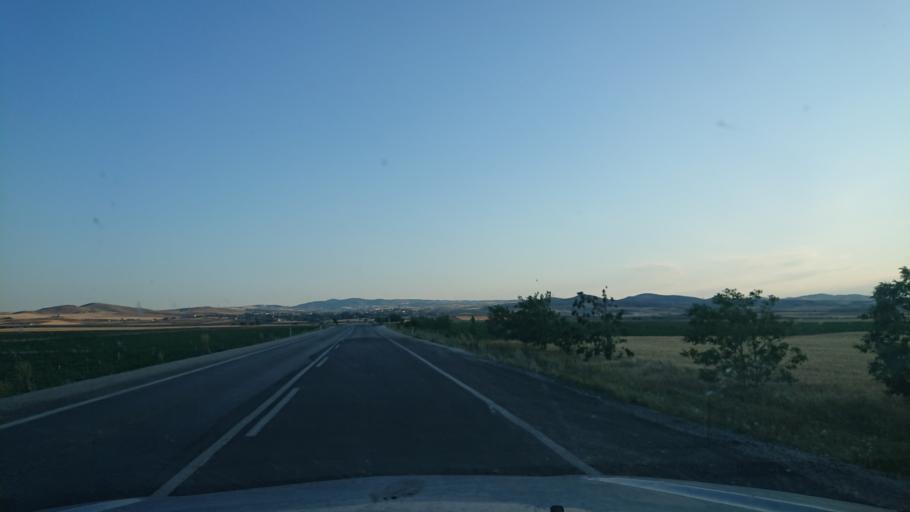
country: TR
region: Aksaray
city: Sariyahsi
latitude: 39.0121
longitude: 33.8657
